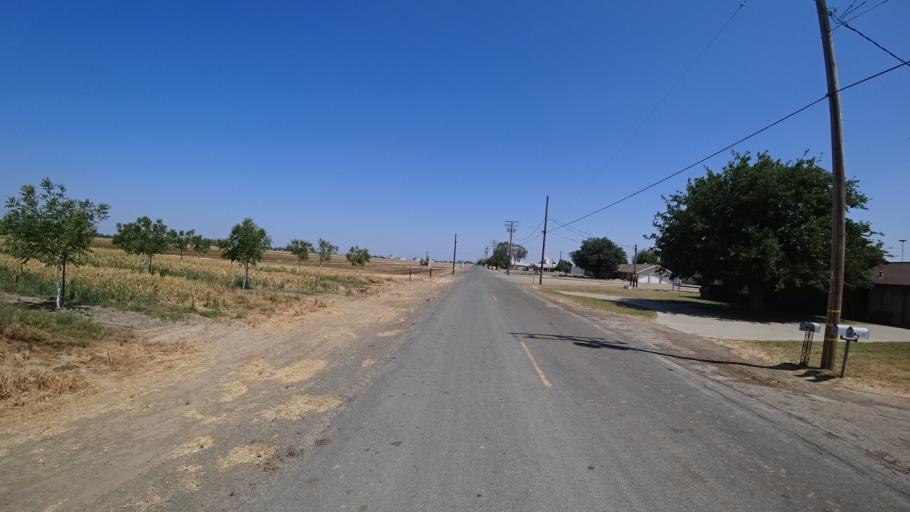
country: US
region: California
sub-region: Kings County
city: Home Garden
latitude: 36.3036
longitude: -119.6100
